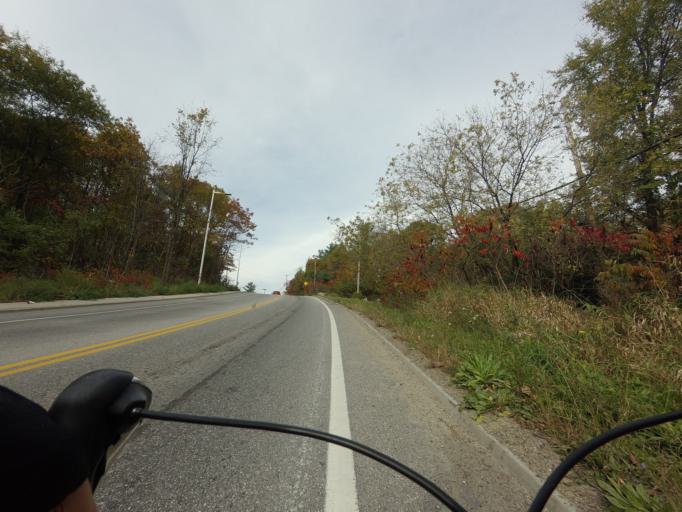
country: CA
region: Quebec
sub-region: Outaouais
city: Val-des-Monts
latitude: 45.6018
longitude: -75.6210
